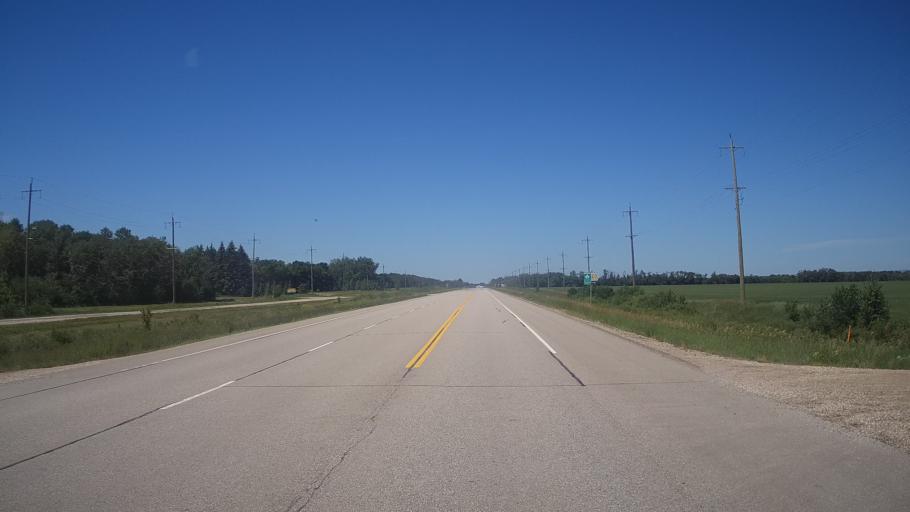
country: CA
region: Manitoba
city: Neepawa
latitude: 50.2253
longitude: -99.3397
